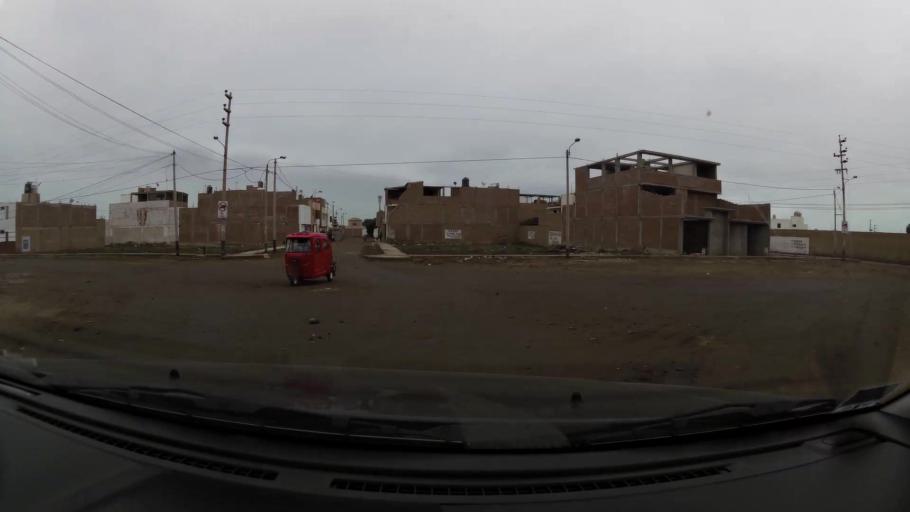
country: PE
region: Ica
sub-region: Provincia de Pisco
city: Pisco
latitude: -13.7110
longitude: -76.2120
